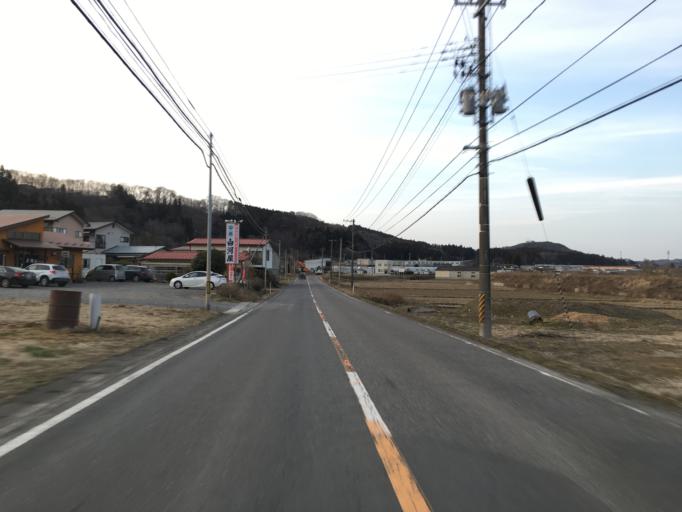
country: JP
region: Ibaraki
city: Daigo
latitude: 36.9363
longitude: 140.4066
